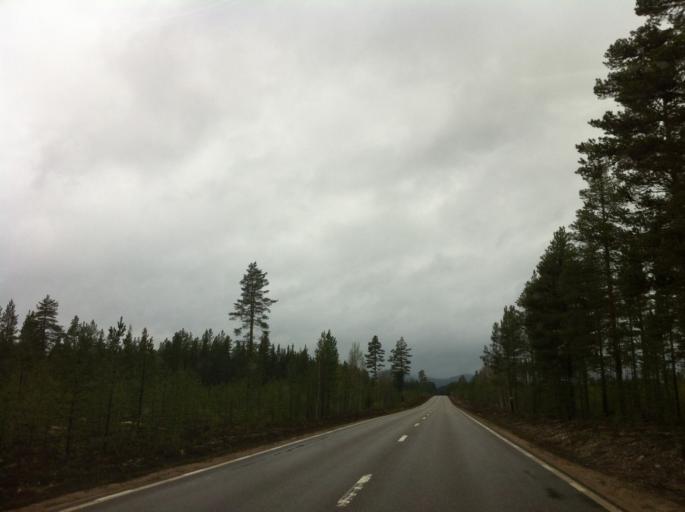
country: SE
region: Jaemtland
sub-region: Harjedalens Kommun
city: Sveg
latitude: 62.1380
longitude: 13.9936
